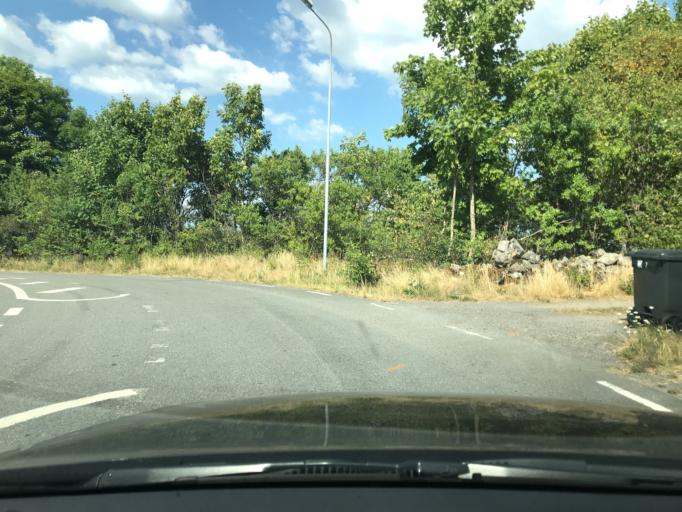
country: SE
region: Skane
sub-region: Hassleholms Kommun
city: Hastveda
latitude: 56.2744
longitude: 13.9129
